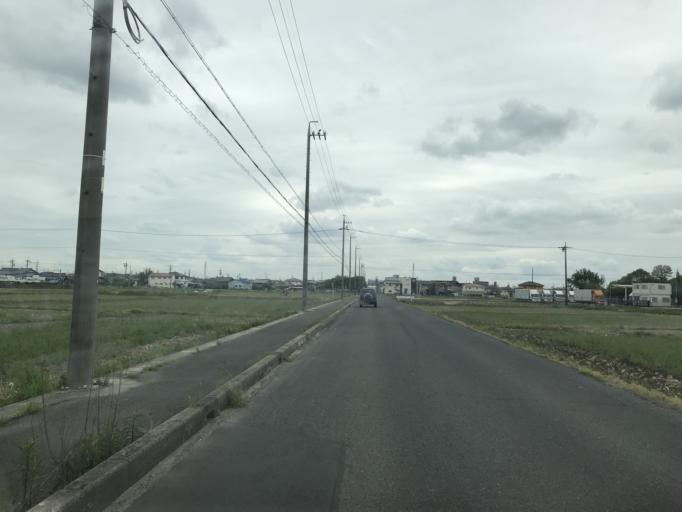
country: JP
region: Aichi
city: Kasugai
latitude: 35.2690
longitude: 136.9682
